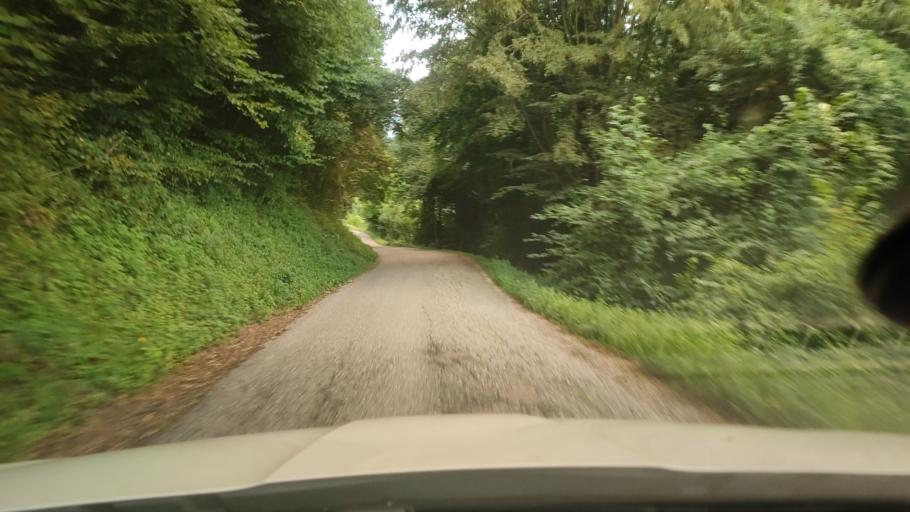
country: IT
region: Friuli Venezia Giulia
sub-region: Provincia di Udine
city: Cras
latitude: 46.2164
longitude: 13.6448
